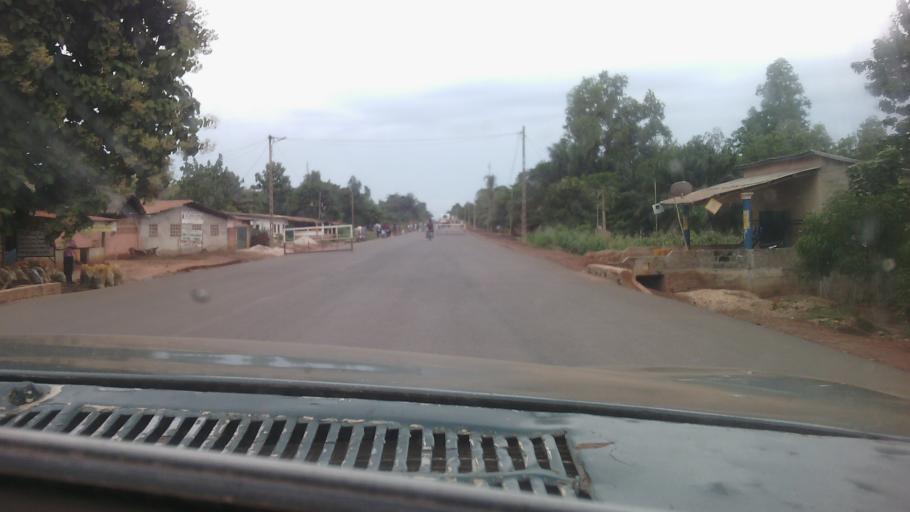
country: BJ
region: Mono
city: Come
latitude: 6.5248
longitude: 1.8185
